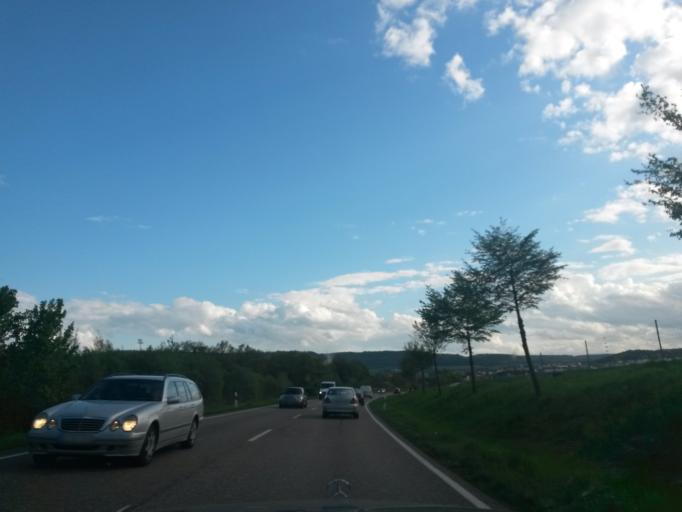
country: DE
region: Baden-Wuerttemberg
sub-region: Regierungsbezirk Stuttgart
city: Aalen
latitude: 48.8463
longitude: 10.0703
